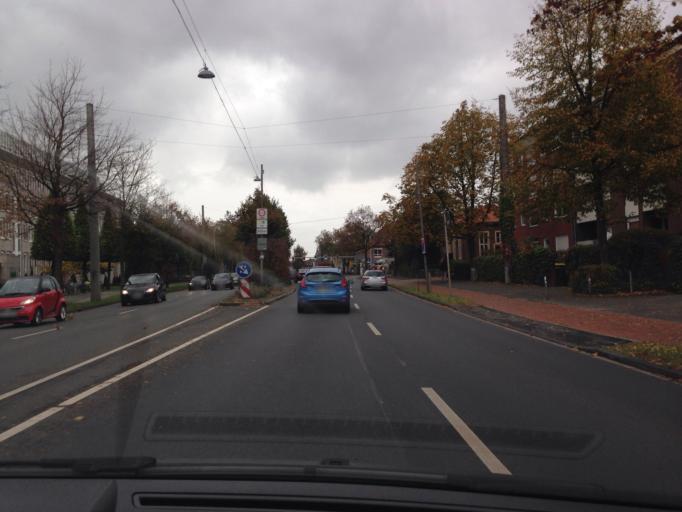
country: DE
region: North Rhine-Westphalia
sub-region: Regierungsbezirk Munster
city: Muenster
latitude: 51.9482
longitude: 7.6155
